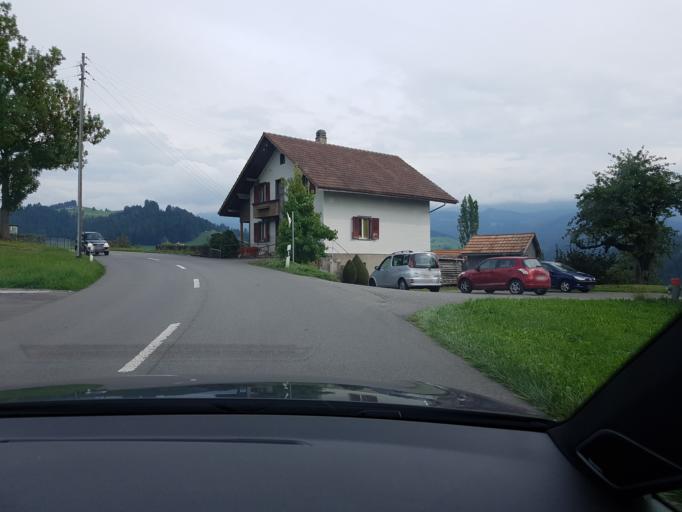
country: CH
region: Bern
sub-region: Thun District
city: Buchholterberg
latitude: 46.7942
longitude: 7.7121
